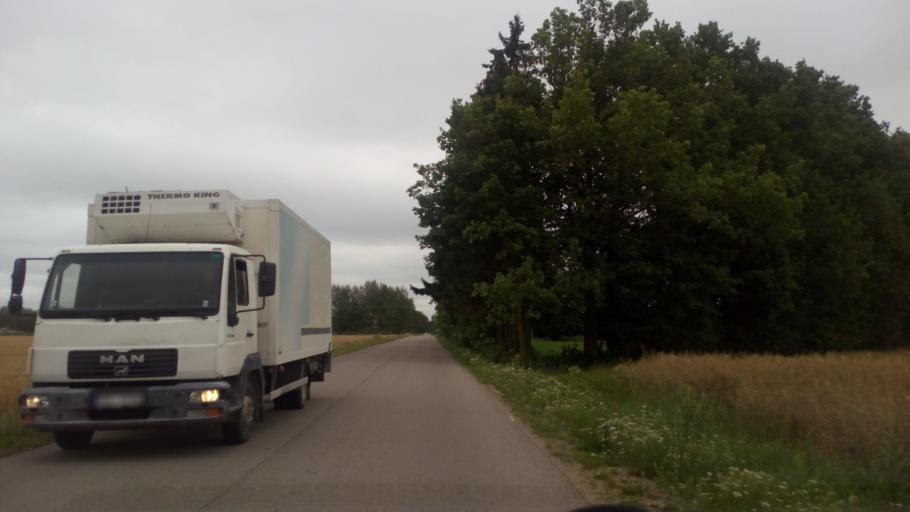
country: LV
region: Rundales
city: Pilsrundale
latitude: 56.4309
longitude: 23.9750
